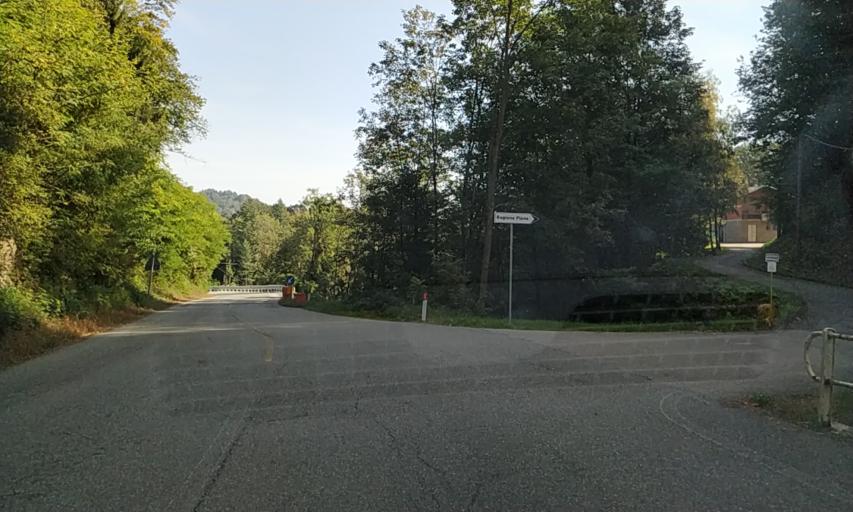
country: IT
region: Piedmont
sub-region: Provincia di Biella
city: Portula
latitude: 45.6779
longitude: 8.1795
